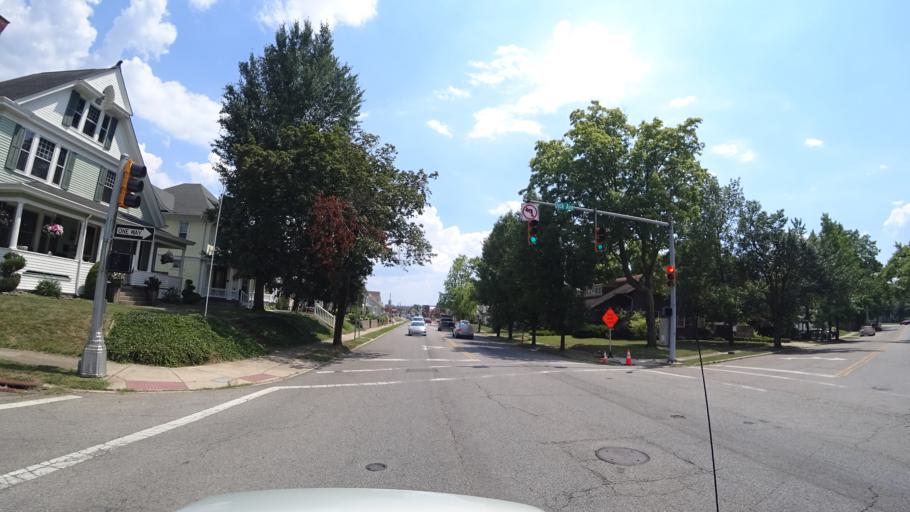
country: US
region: Ohio
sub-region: Butler County
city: Hamilton
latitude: 39.4083
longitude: -84.5754
